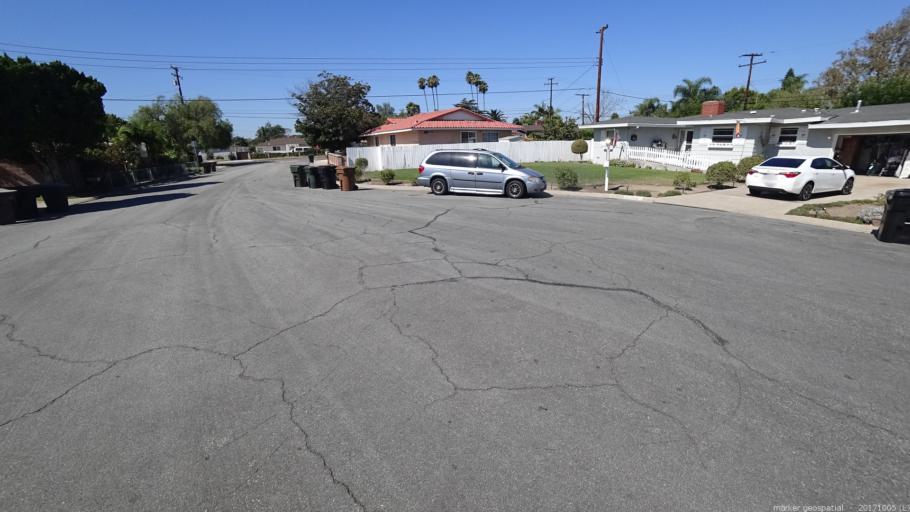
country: US
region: California
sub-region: Orange County
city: Garden Grove
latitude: 33.7827
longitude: -117.9665
